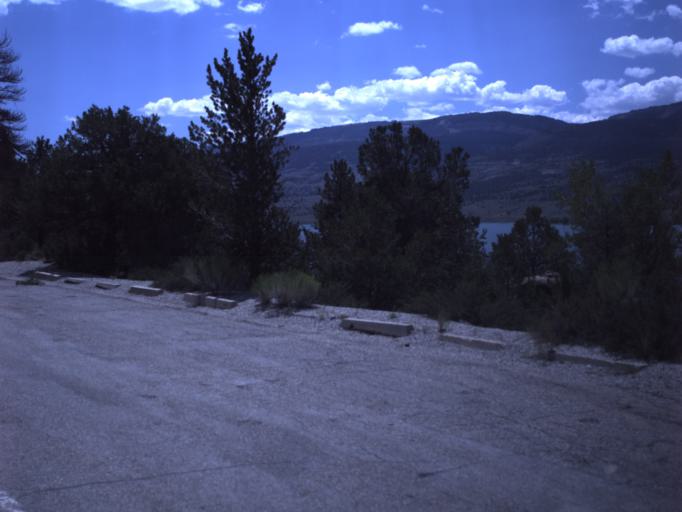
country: US
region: Utah
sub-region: Emery County
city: Orangeville
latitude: 39.3011
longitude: -111.2721
